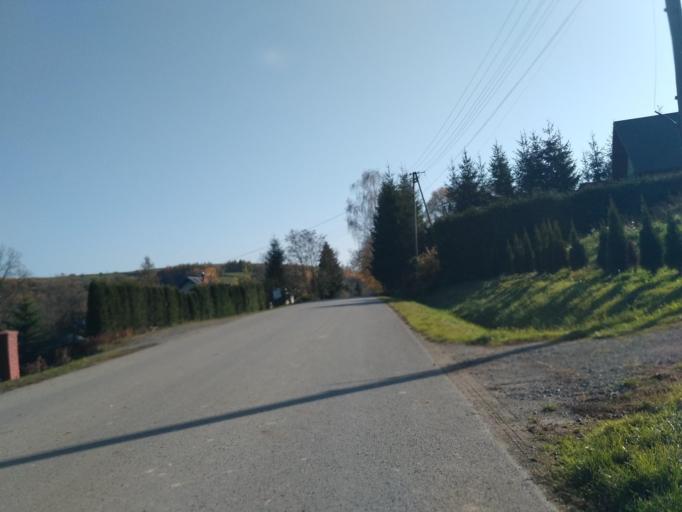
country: PL
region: Subcarpathian Voivodeship
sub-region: Powiat brzozowski
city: Nozdrzec
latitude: 49.8031
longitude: 22.1697
